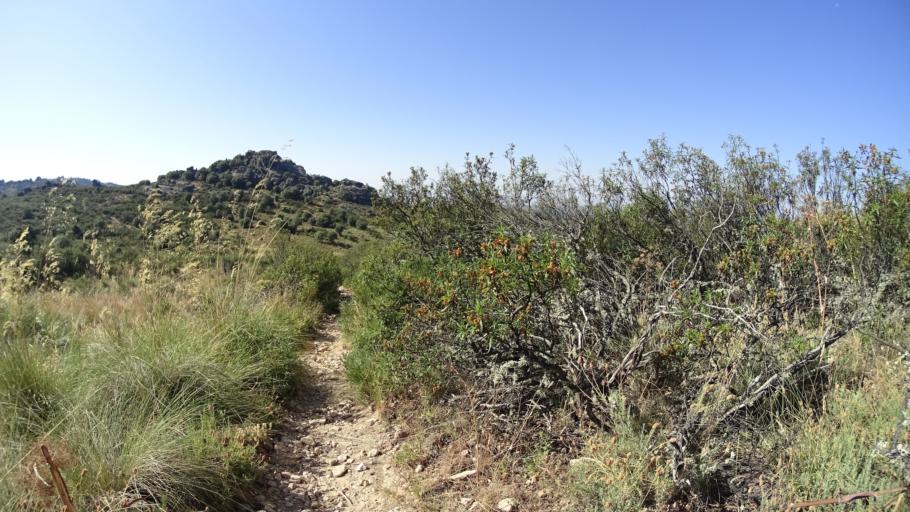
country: ES
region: Madrid
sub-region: Provincia de Madrid
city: Hoyo de Manzanares
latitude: 40.6485
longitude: -3.9386
